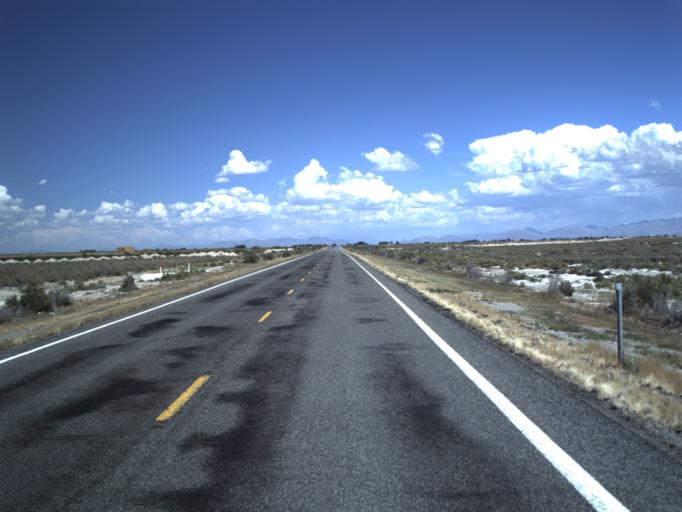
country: US
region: Utah
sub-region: Millard County
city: Delta
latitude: 39.3218
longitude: -112.7383
